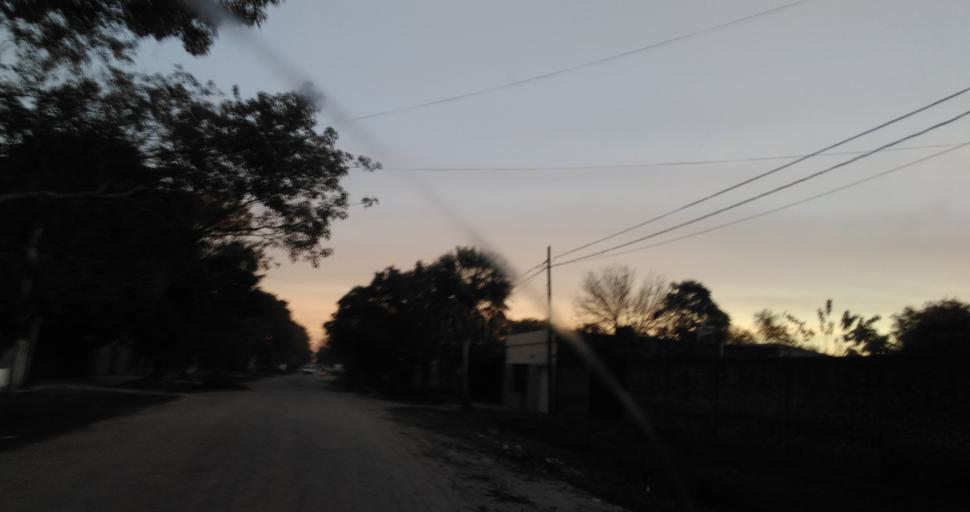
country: AR
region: Chaco
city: Resistencia
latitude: -27.4765
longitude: -58.9919
